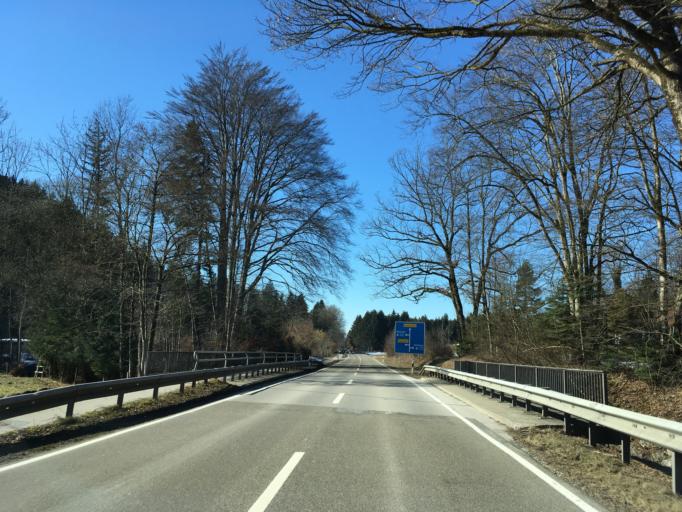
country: DE
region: Bavaria
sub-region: Upper Bavaria
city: Samerberg
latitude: 47.7957
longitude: 12.2181
